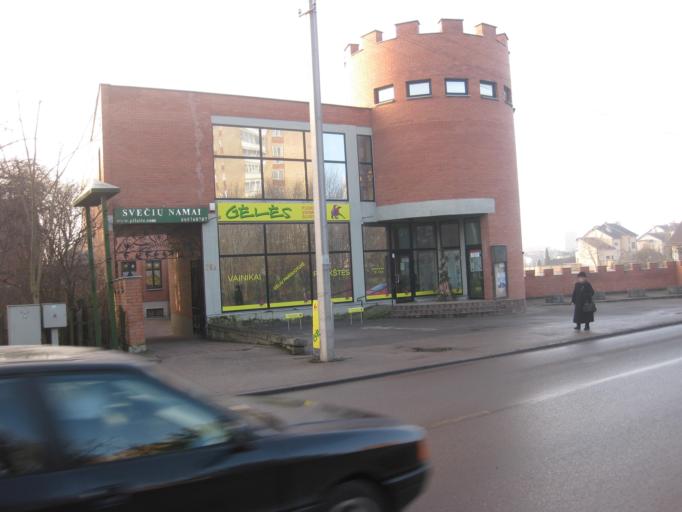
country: LT
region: Kauno apskritis
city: Dainava (Kaunas)
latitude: 54.9053
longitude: 23.9730
